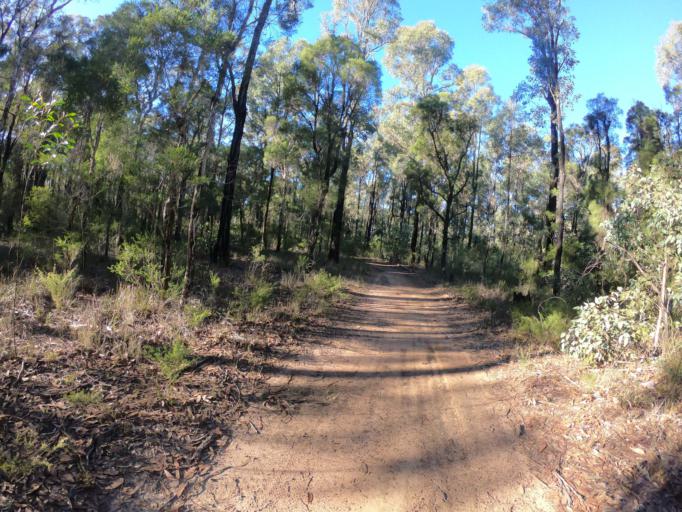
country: AU
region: New South Wales
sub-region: Hawkesbury
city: South Windsor
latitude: -33.6450
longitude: 150.7972
